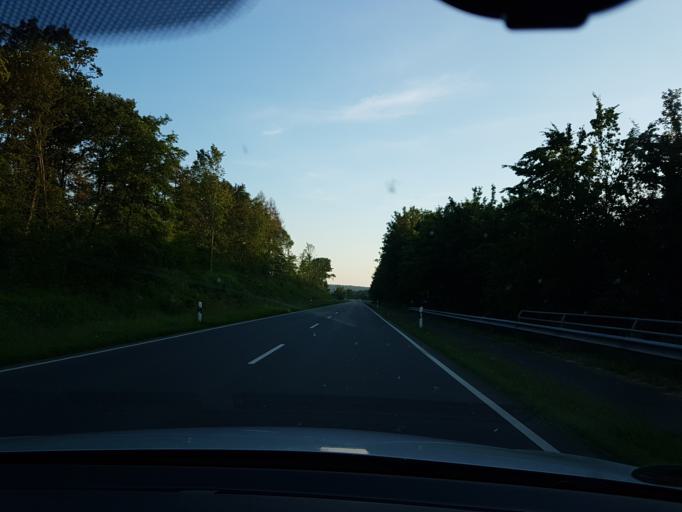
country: DE
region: Lower Saxony
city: Wolsdorf
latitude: 52.1822
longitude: 10.9758
